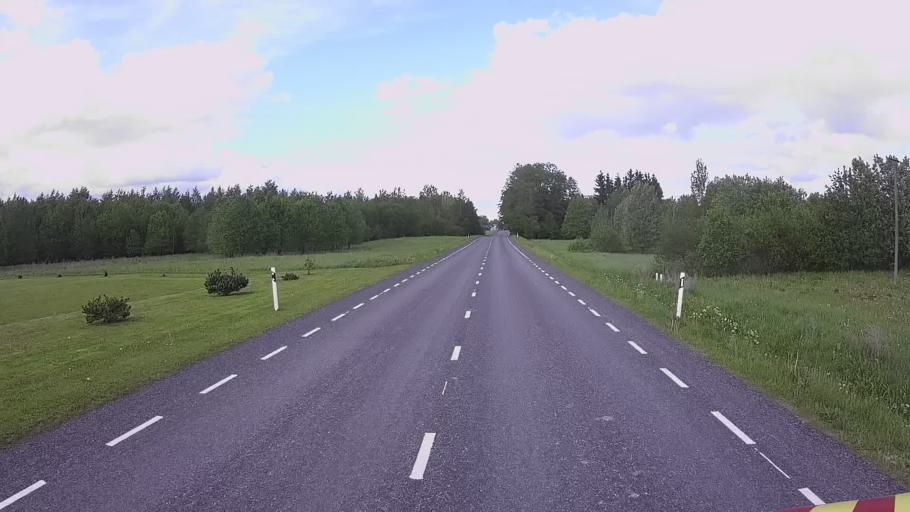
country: EE
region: Jogevamaa
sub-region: Mustvee linn
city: Mustvee
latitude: 58.9931
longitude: 26.8872
